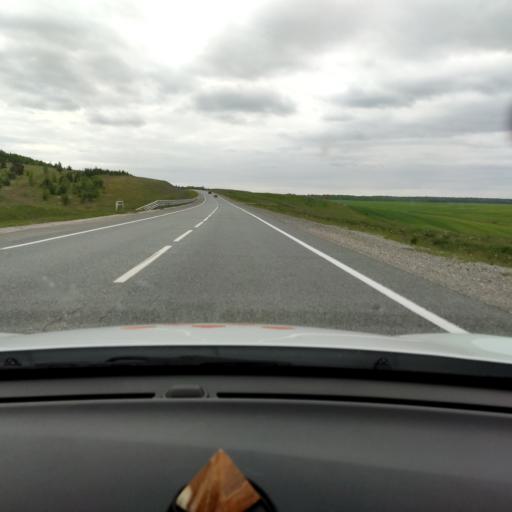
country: RU
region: Tatarstan
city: Pestretsy
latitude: 55.6452
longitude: 49.6862
